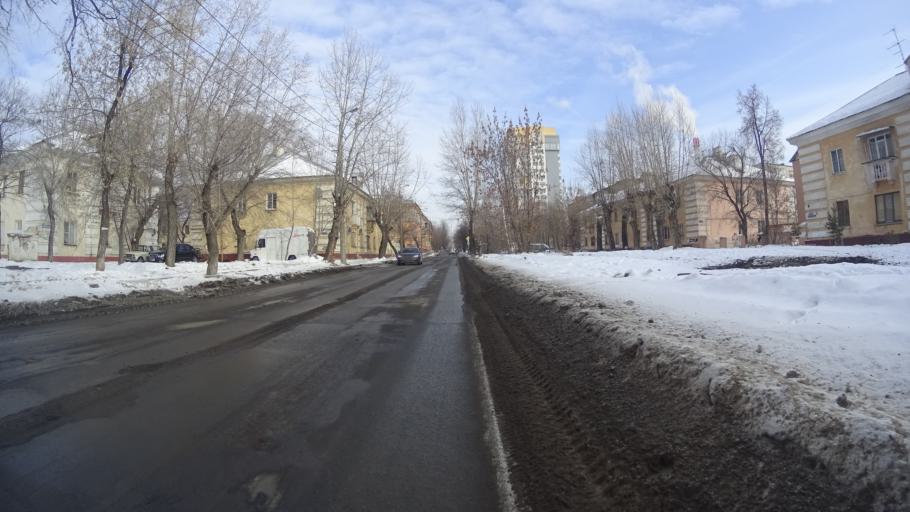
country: RU
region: Chelyabinsk
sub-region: Gorod Chelyabinsk
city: Chelyabinsk
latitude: 55.1521
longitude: 61.3694
